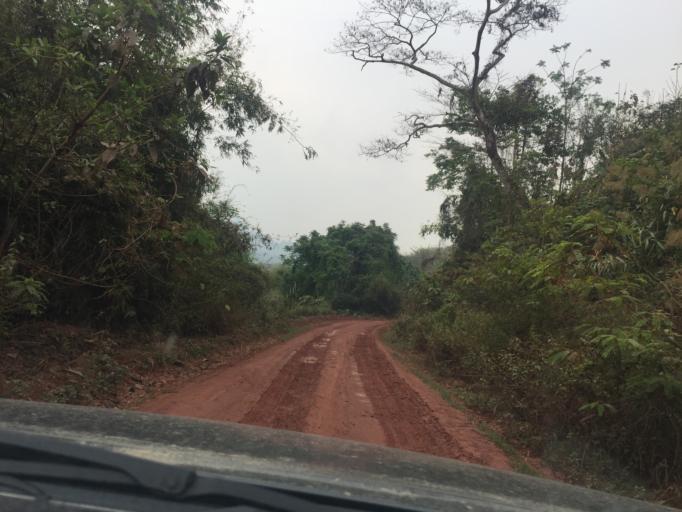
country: TH
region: Nan
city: Bo Kluea
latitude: 18.8457
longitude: 101.4108
